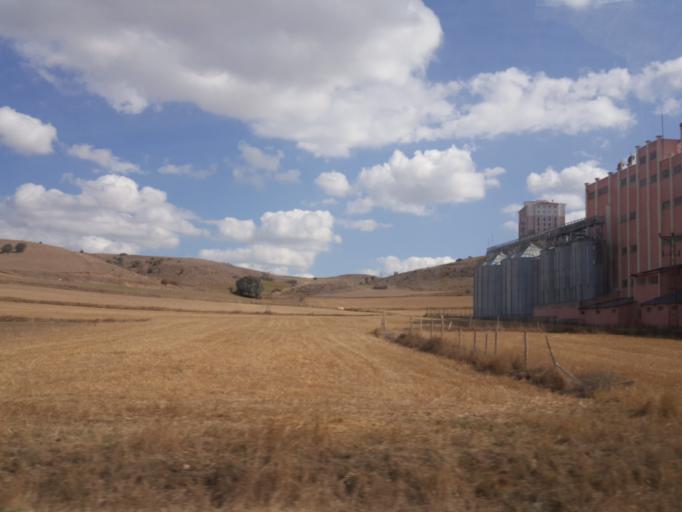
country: TR
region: Tokat
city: Artova
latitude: 40.1176
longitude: 36.3127
